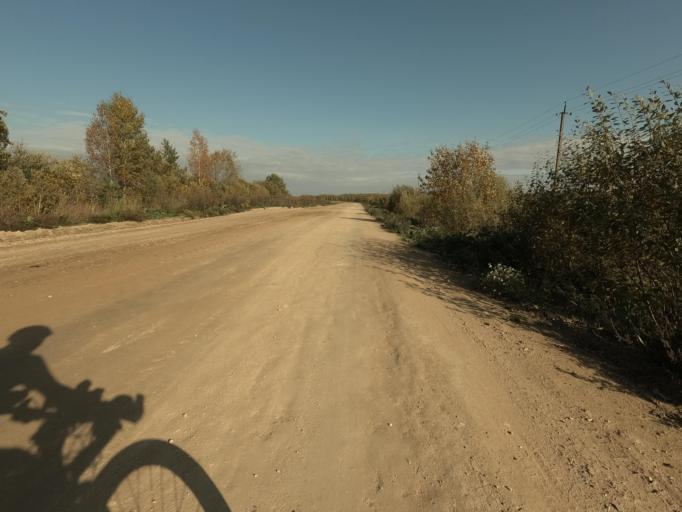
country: RU
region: Novgorod
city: Batetskiy
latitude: 58.8175
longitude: 30.7003
